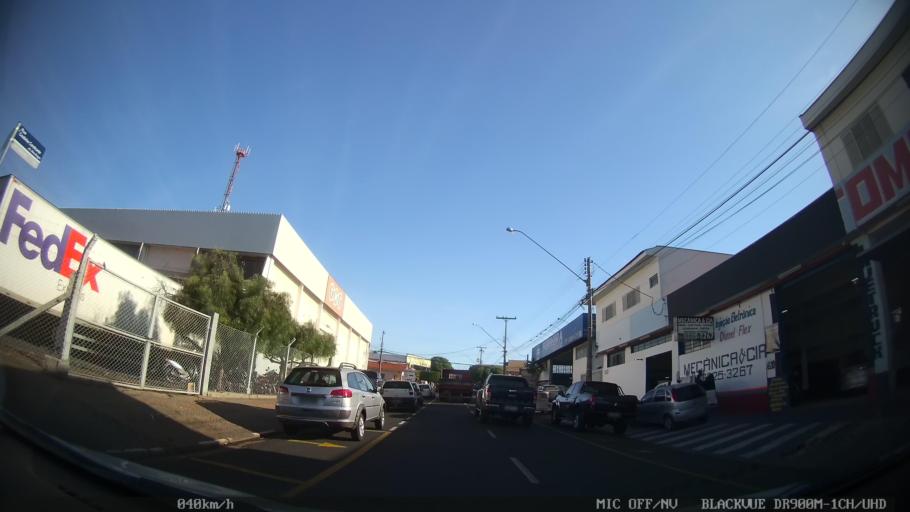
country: BR
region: Sao Paulo
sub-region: Sao Jose Do Rio Preto
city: Sao Jose do Rio Preto
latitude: -20.7884
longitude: -49.3579
